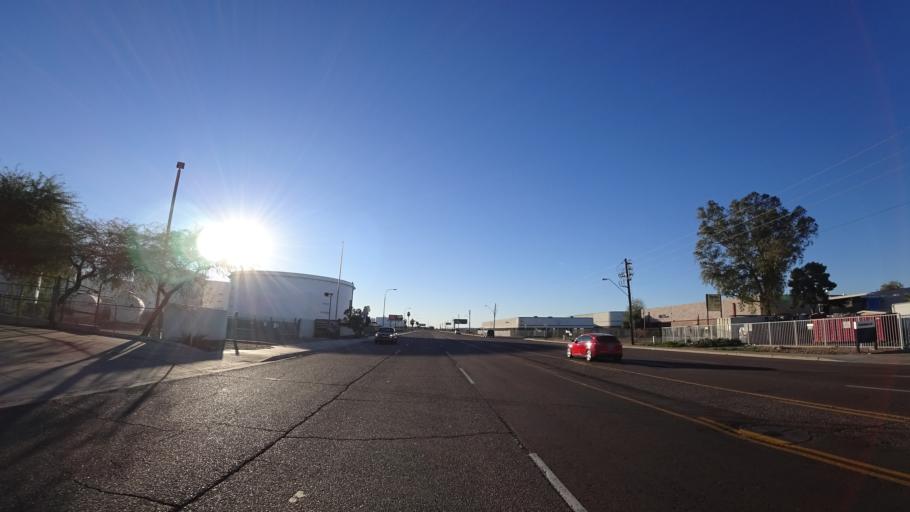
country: US
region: Arizona
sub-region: Maricopa County
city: Tolleson
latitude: 33.4512
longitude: -112.1713
